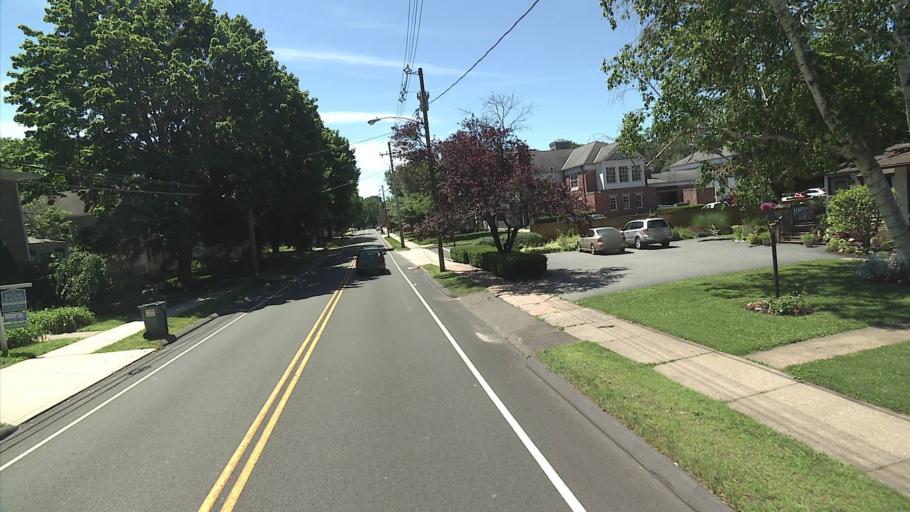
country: US
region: Connecticut
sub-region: New Haven County
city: Guilford
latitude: 41.2861
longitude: -72.6831
